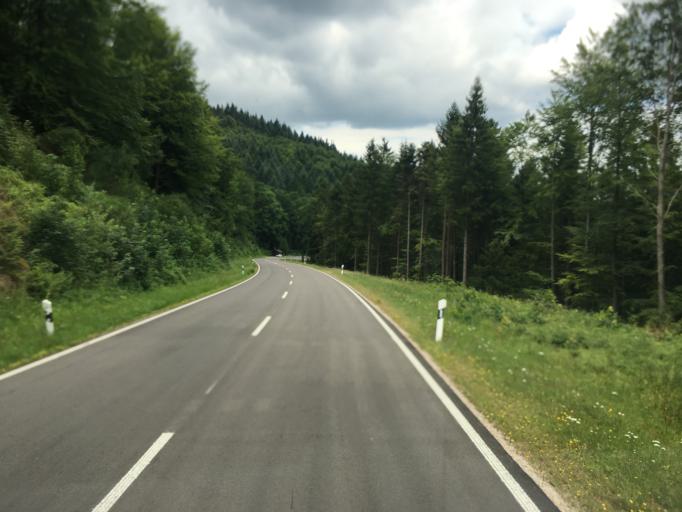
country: DE
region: Baden-Wuerttemberg
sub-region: Karlsruhe Region
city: Buhlertal
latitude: 48.7067
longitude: 8.2365
